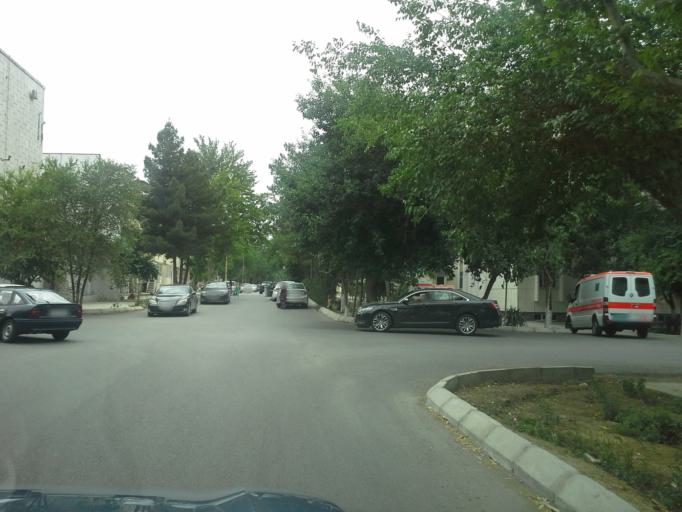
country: TM
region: Ahal
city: Ashgabat
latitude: 37.9170
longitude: 58.4055
